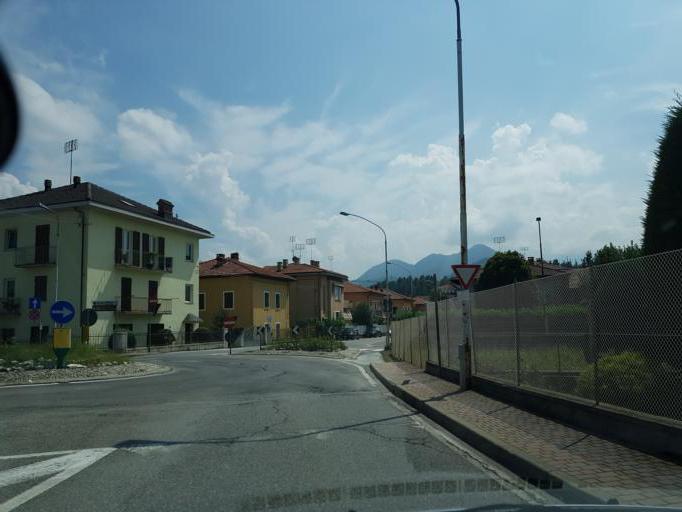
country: IT
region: Piedmont
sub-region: Provincia di Cuneo
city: Borgo San Dalmazzo
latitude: 44.3333
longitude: 7.4844
